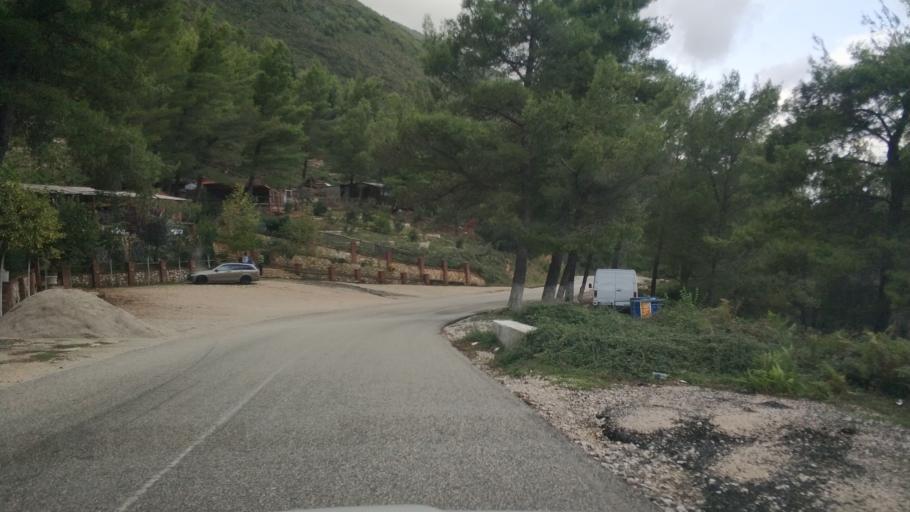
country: AL
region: Vlore
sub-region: Rrethi i Vlores
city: Orikum
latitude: 40.2538
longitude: 19.5355
